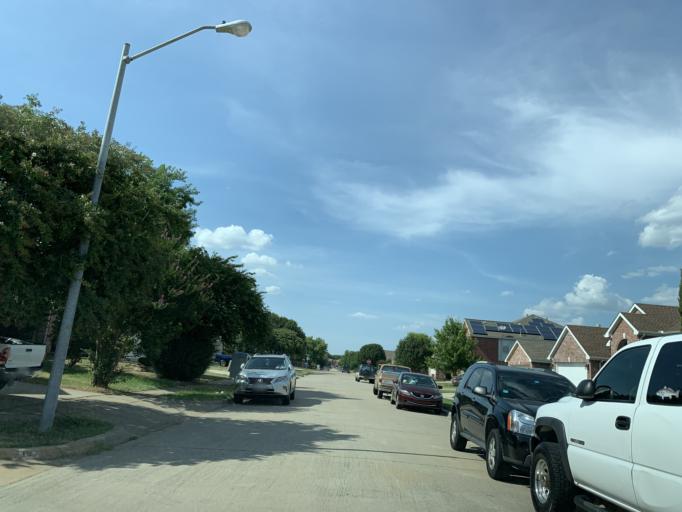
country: US
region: Texas
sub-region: Dallas County
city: Cedar Hill
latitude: 32.6479
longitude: -97.0100
